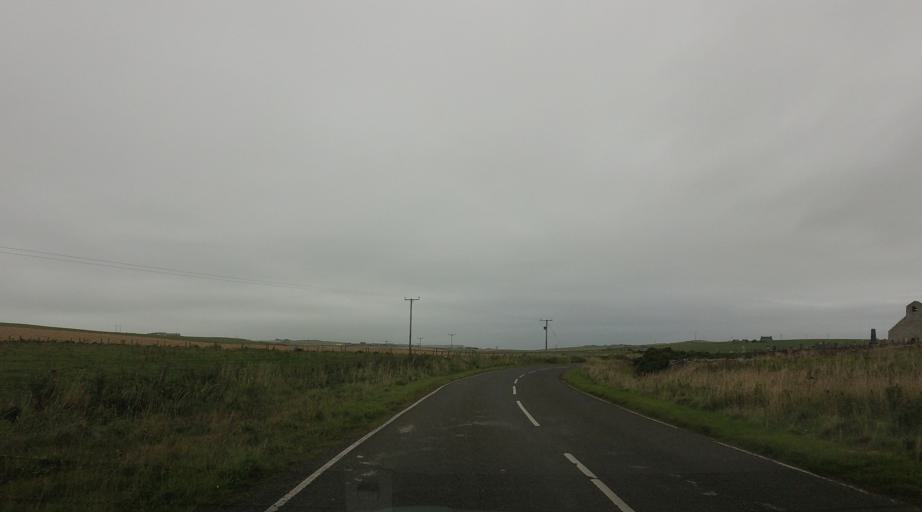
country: GB
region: Scotland
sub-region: Orkney Islands
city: Orkney
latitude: 58.7421
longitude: -2.9711
